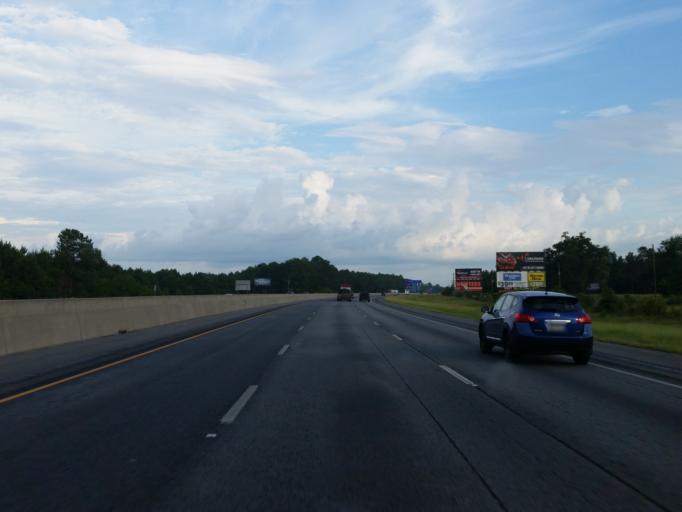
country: US
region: Georgia
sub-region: Lowndes County
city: Remerton
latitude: 30.8745
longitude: -83.3422
